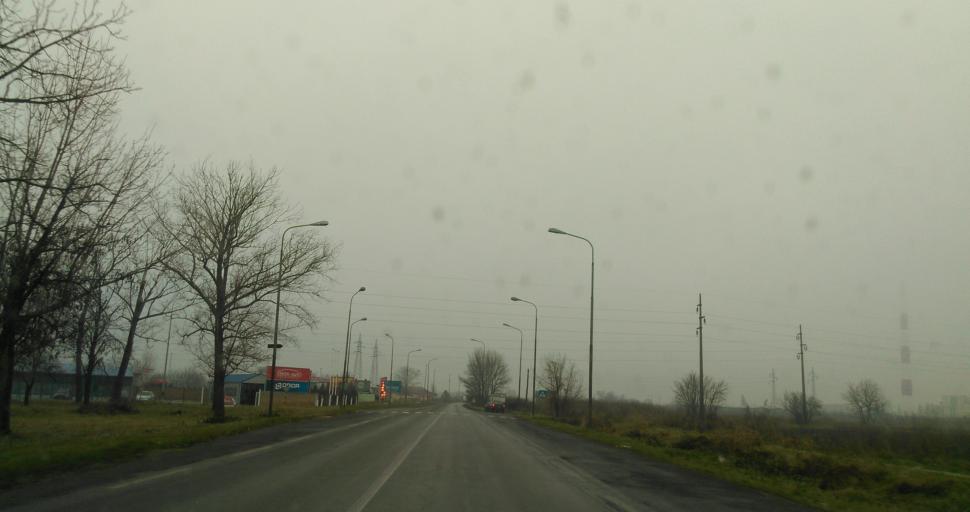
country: RS
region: Autonomna Pokrajina Vojvodina
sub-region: Srednjebanatski Okrug
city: Zrenjanin
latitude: 45.3653
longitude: 20.4227
